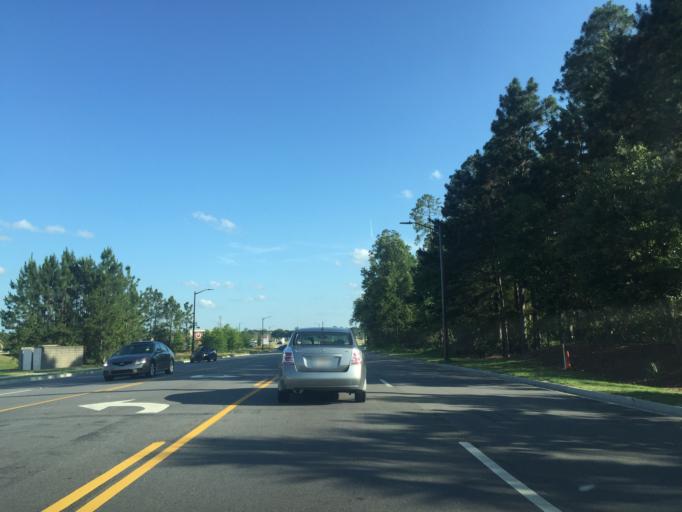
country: US
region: Georgia
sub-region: Chatham County
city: Pooler
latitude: 32.1395
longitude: -81.2470
